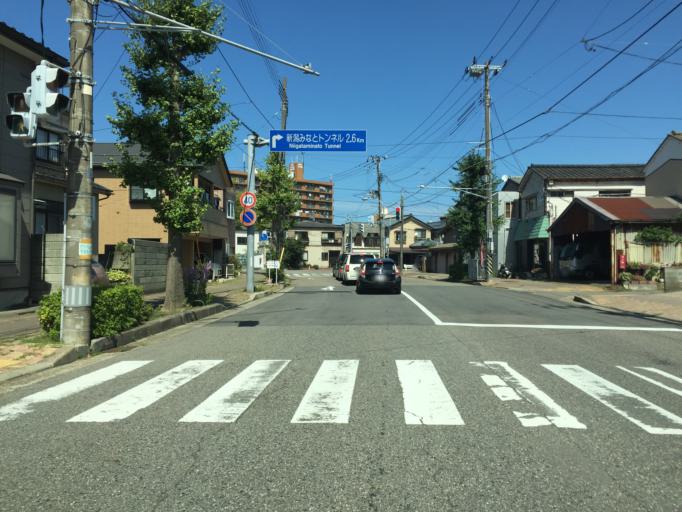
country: JP
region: Niigata
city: Niigata-shi
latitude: 37.9304
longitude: 139.0473
